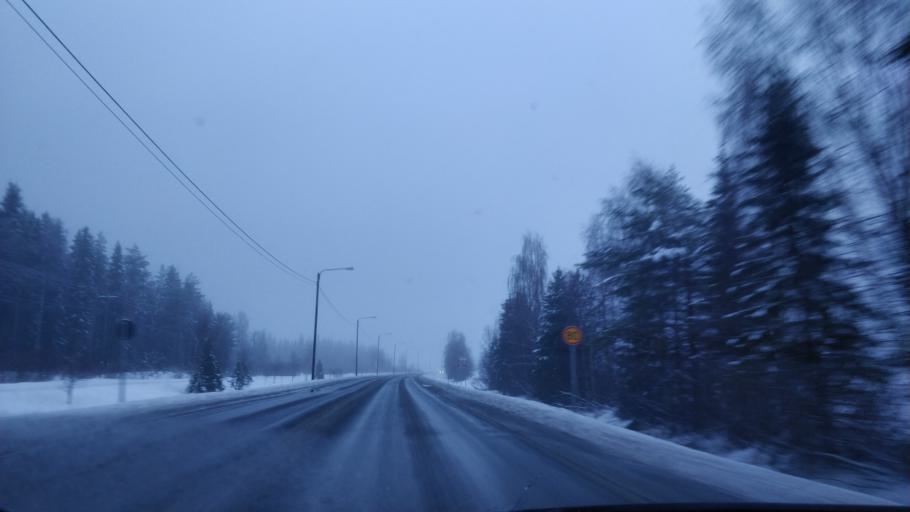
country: FI
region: Lapland
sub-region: Kemi-Tornio
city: Tervola
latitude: 66.1486
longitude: 24.9731
